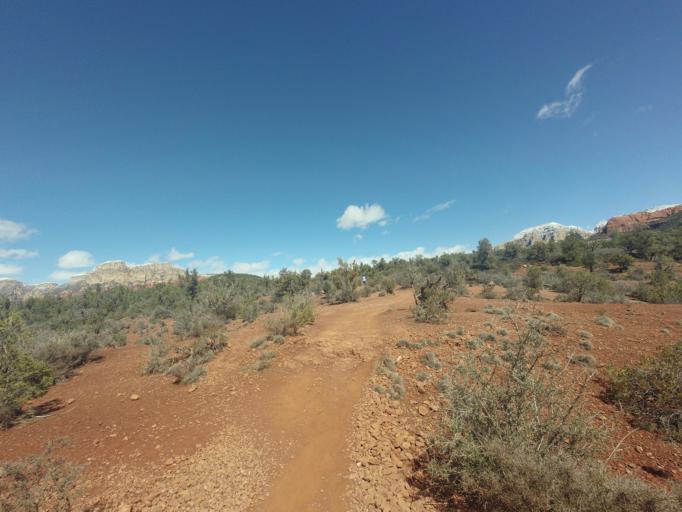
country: US
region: Arizona
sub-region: Yavapai County
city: West Sedona
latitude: 34.9020
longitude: -111.8207
